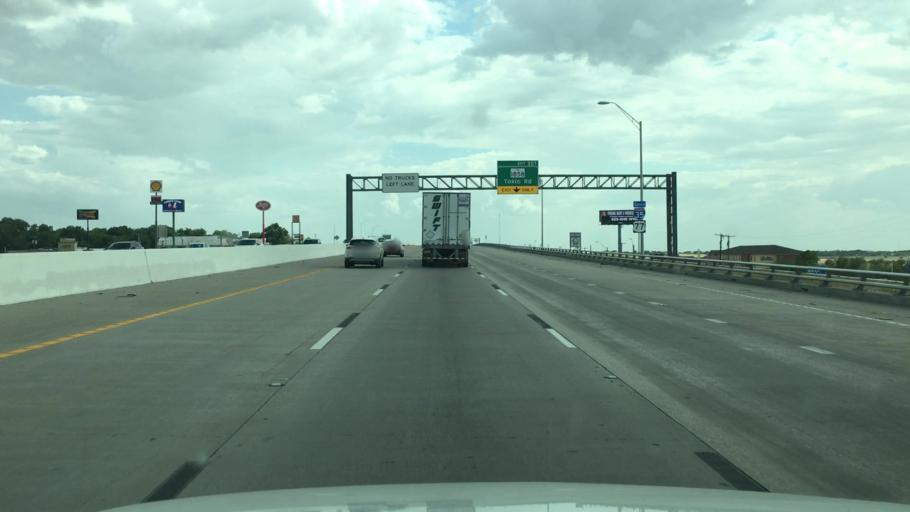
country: US
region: Texas
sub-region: McLennan County
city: West
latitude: 31.8056
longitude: -97.0997
